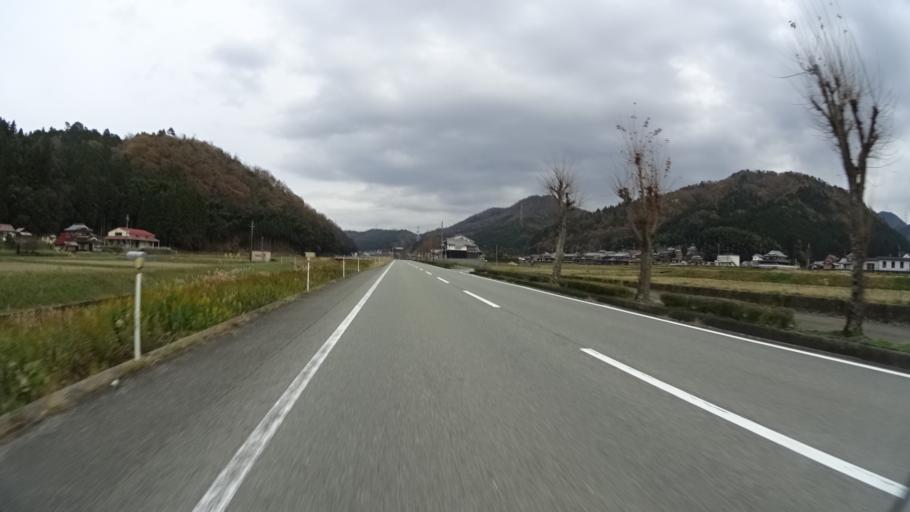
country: JP
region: Hyogo
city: Sasayama
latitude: 35.0741
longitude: 135.3555
